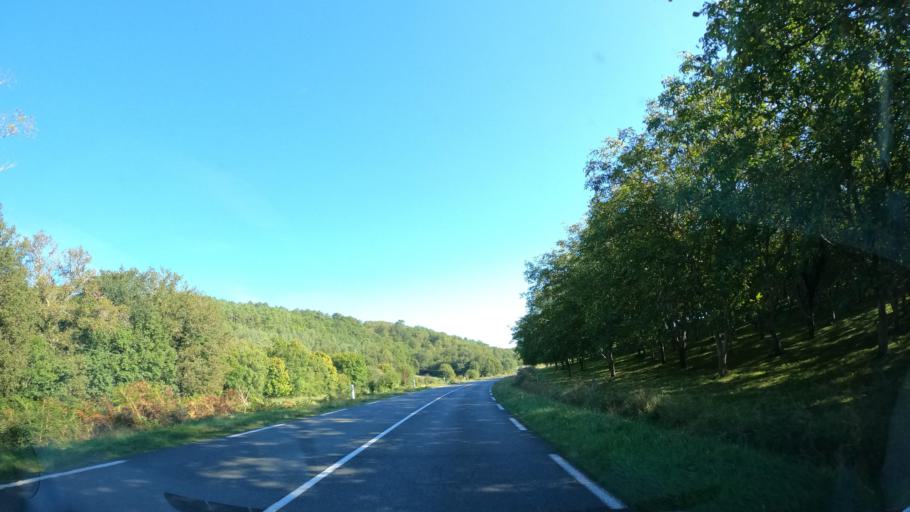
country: FR
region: Aquitaine
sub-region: Departement de la Dordogne
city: Vergt
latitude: 45.0571
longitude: 0.6554
